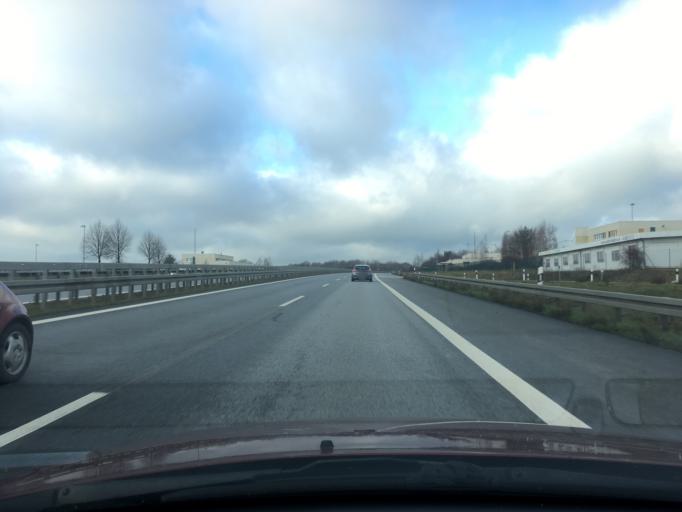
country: DE
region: Saxony
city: Goerlitz
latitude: 51.1858
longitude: 14.9930
